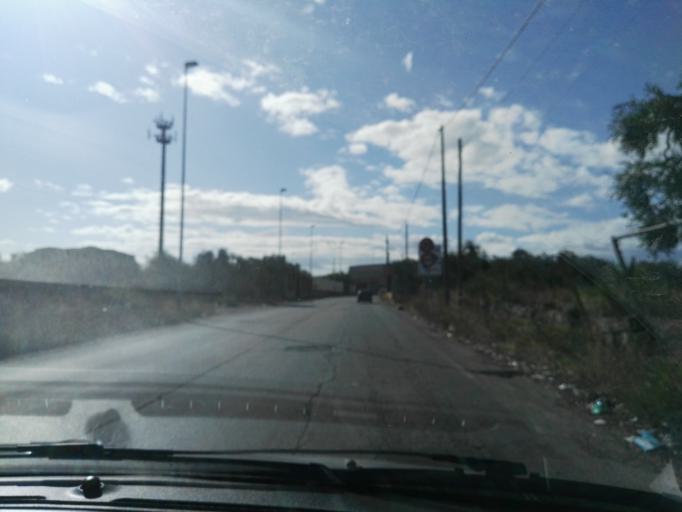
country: IT
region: Apulia
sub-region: Provincia di Bari
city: Triggiano
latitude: 41.0624
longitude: 16.9351
